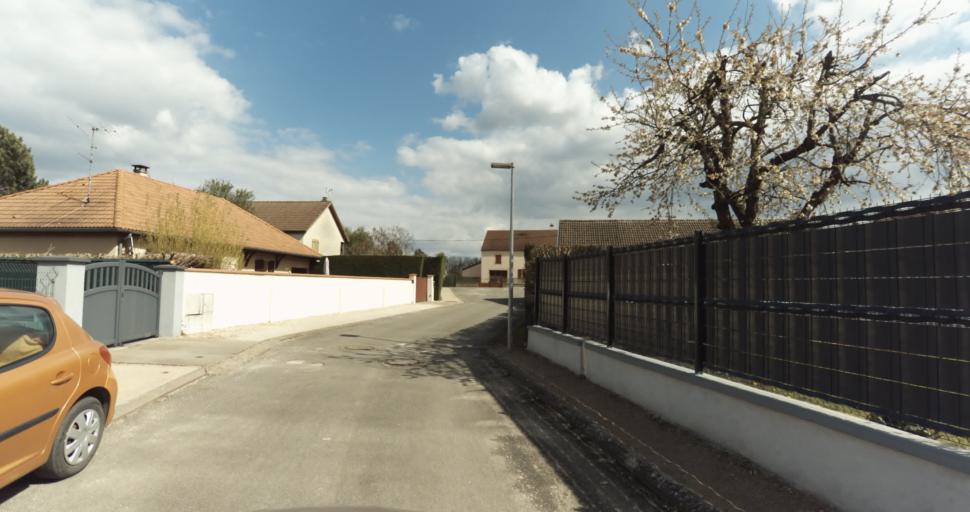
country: FR
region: Bourgogne
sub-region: Departement de la Cote-d'Or
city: Auxonne
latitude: 47.1903
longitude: 5.4007
